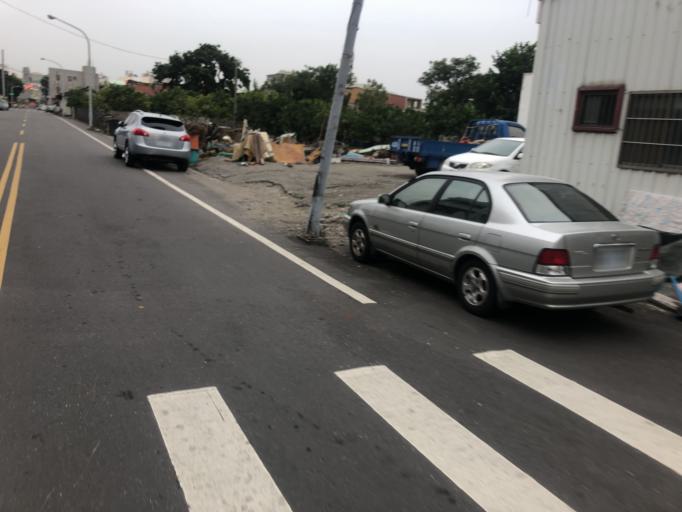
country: TW
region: Taiwan
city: Xinying
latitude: 23.1813
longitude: 120.2443
